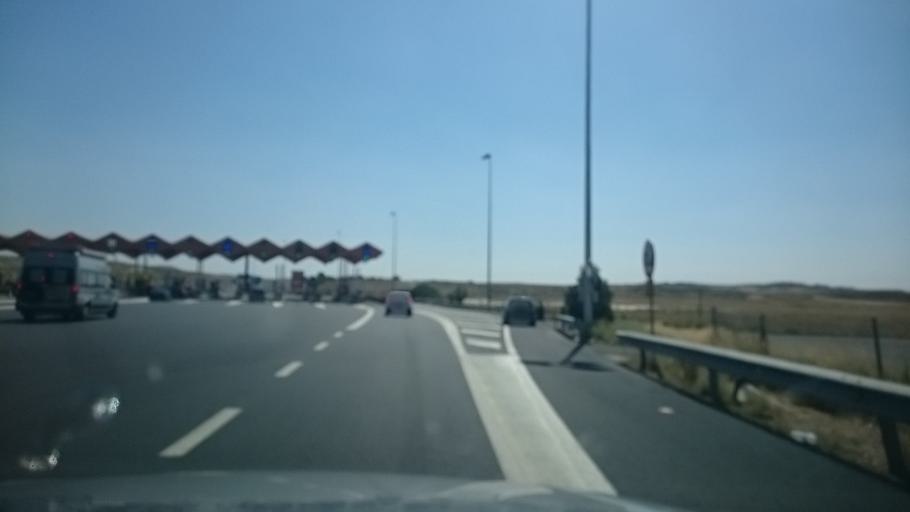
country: ES
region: Aragon
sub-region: Provincia de Zaragoza
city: Pina de Ebro
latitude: 41.5258
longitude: -0.4695
